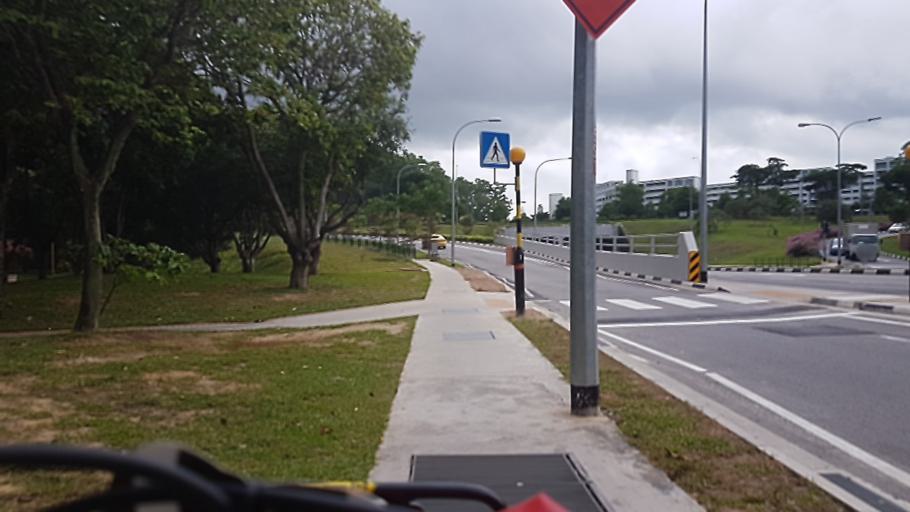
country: SG
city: Singapore
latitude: 1.3509
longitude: 103.9560
